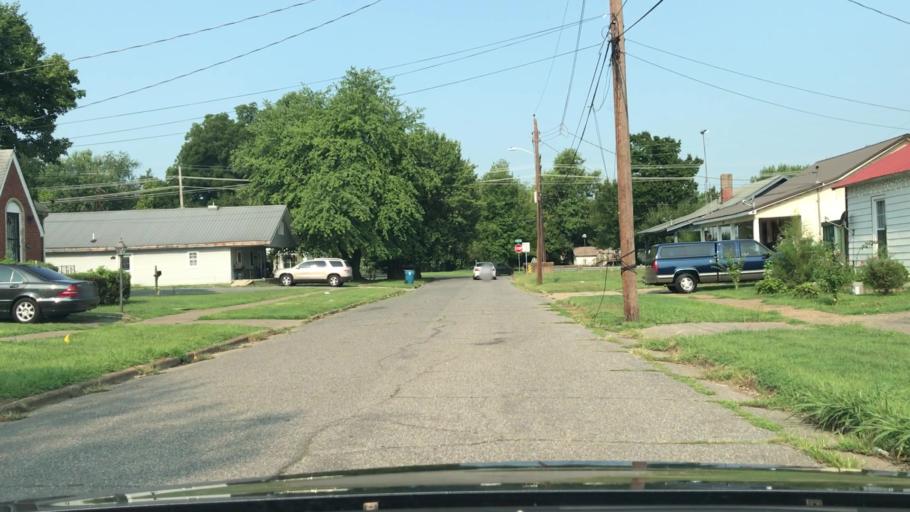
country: US
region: Kentucky
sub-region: Graves County
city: Mayfield
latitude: 36.7359
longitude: -88.6377
